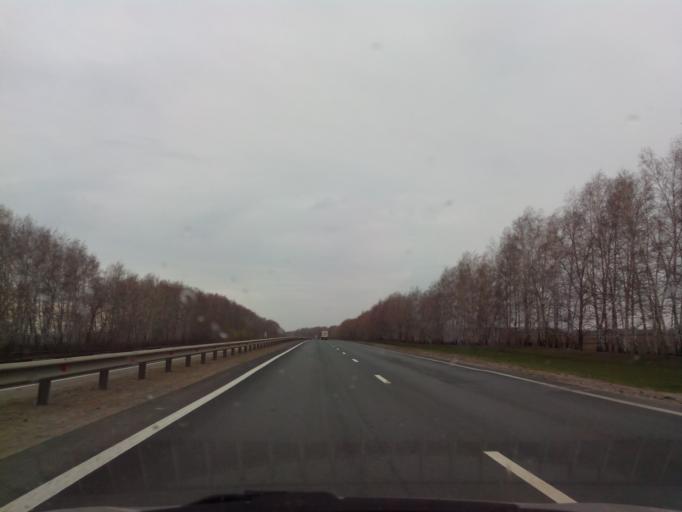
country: RU
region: Tambov
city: Selezni
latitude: 52.7637
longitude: 41.1156
